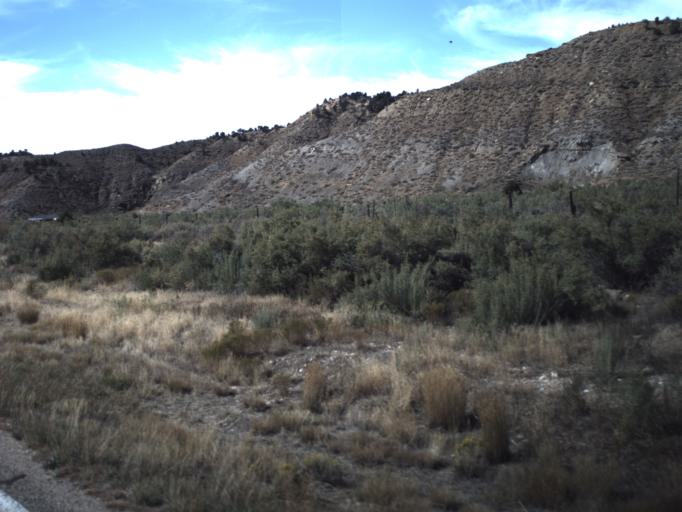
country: US
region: Utah
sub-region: Garfield County
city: Panguitch
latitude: 37.6017
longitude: -112.0608
